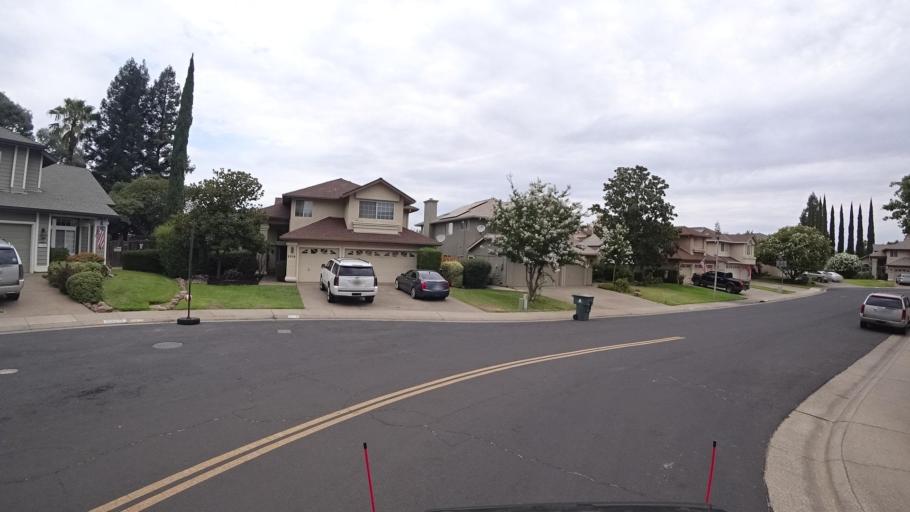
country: US
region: California
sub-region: Placer County
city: Rocklin
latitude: 38.7859
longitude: -121.2653
